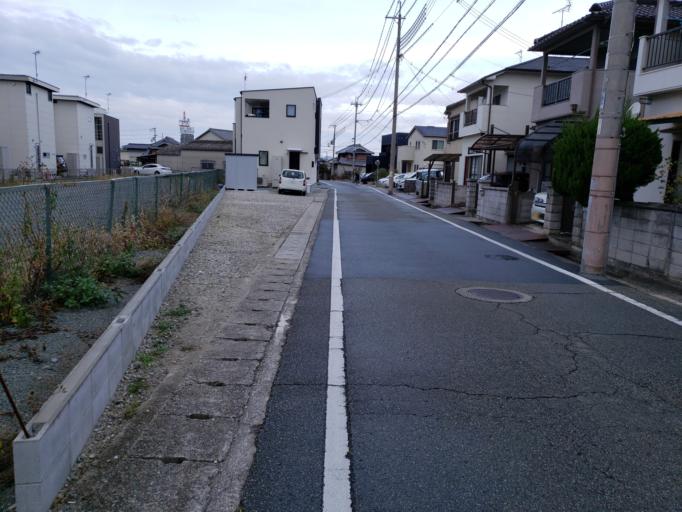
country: JP
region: Hyogo
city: Kakogawacho-honmachi
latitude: 34.7562
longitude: 134.8463
